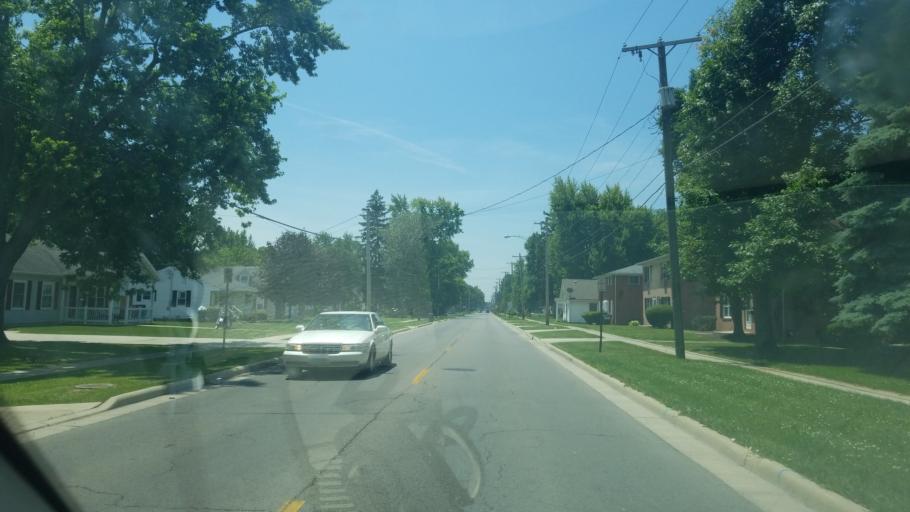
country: US
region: Ohio
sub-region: Hancock County
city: Findlay
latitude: 41.0607
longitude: -83.6359
